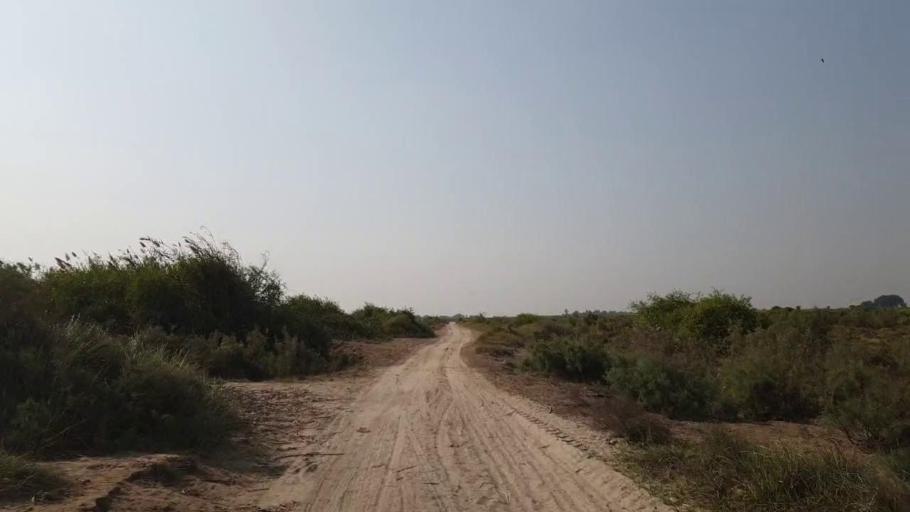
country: PK
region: Sindh
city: Bulri
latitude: 24.9465
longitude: 68.3845
